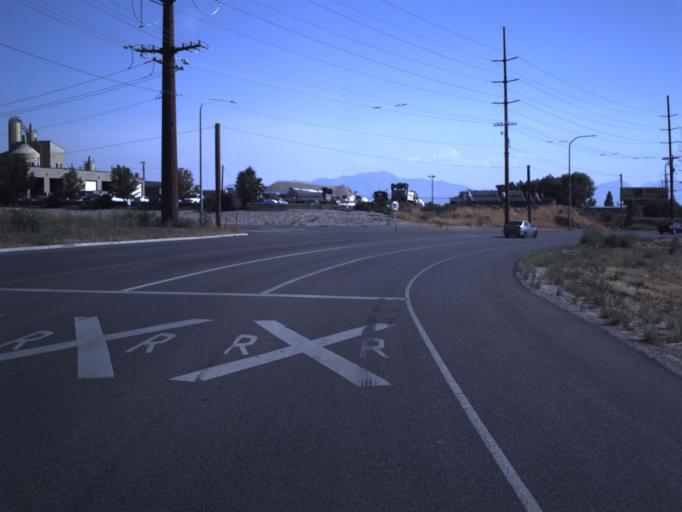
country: US
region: Utah
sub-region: Utah County
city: Orem
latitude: 40.3055
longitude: -111.7334
